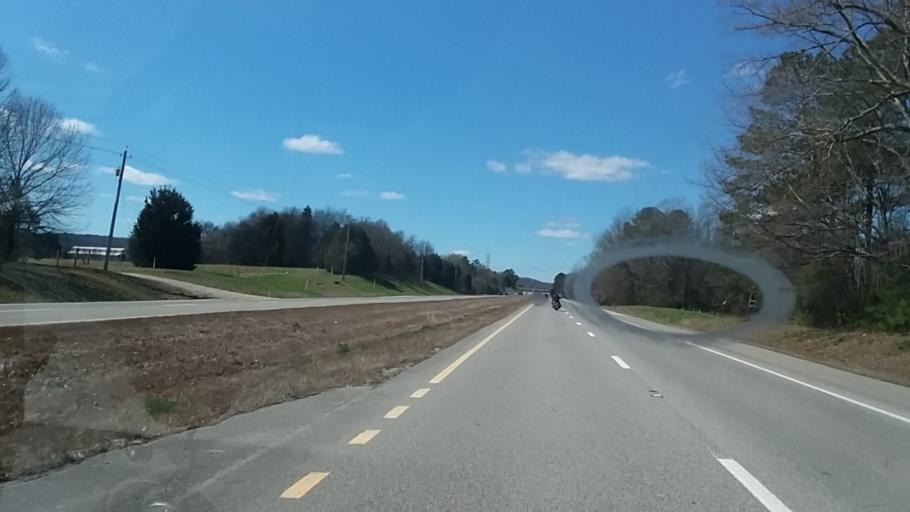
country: US
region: Alabama
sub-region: Colbert County
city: Cherokee
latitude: 34.7329
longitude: -87.8746
